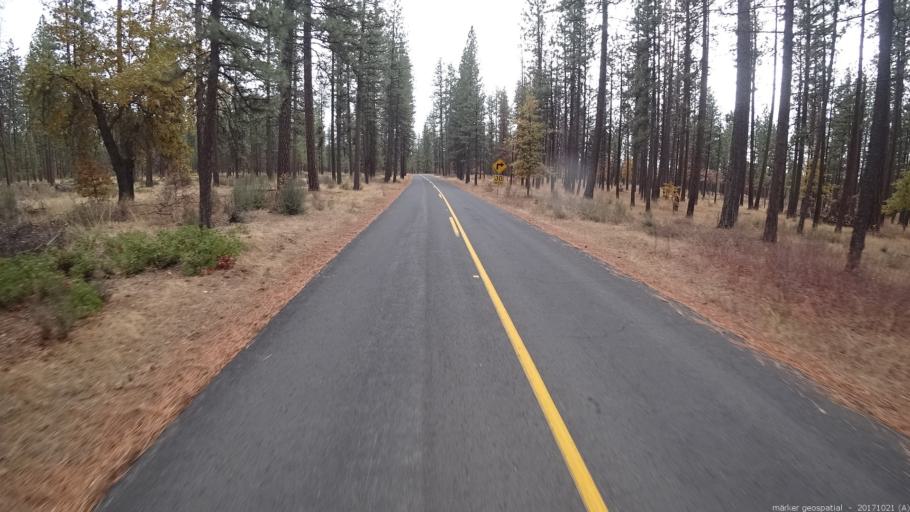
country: US
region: California
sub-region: Shasta County
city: Burney
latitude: 40.9362
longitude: -121.6430
